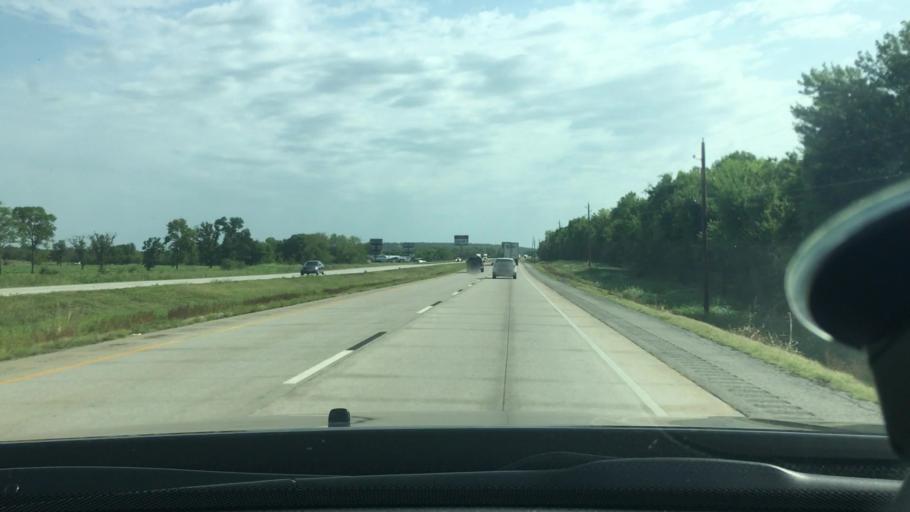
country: US
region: Oklahoma
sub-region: Atoka County
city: Atoka
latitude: 34.4139
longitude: -96.1038
